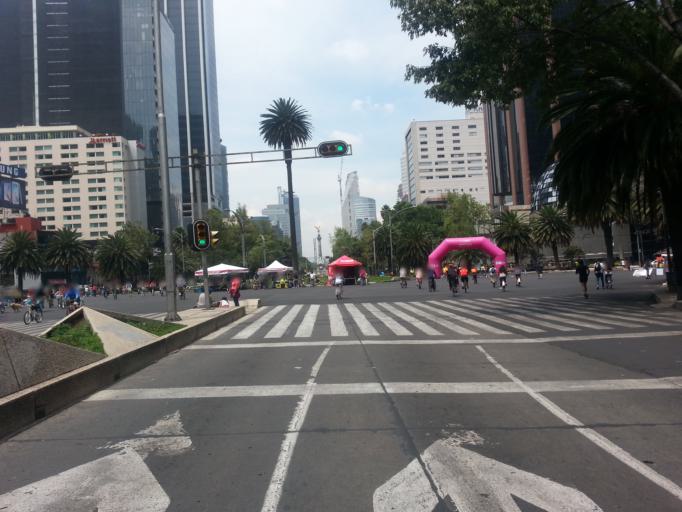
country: MX
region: Mexico City
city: Cuauhtemoc
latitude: 19.4292
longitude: -99.1630
